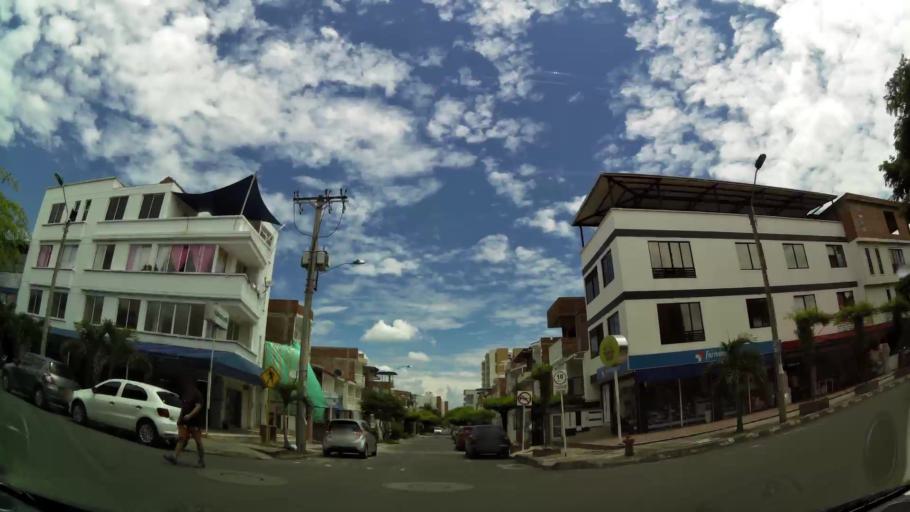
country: CO
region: Valle del Cauca
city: Cali
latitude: 3.3731
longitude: -76.5188
